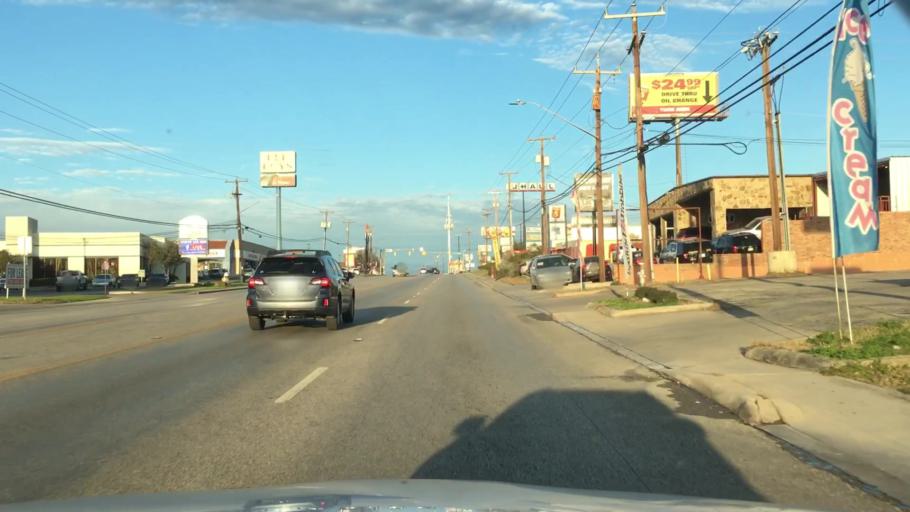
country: US
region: Texas
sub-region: Bexar County
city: Windcrest
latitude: 29.5532
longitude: -98.4039
